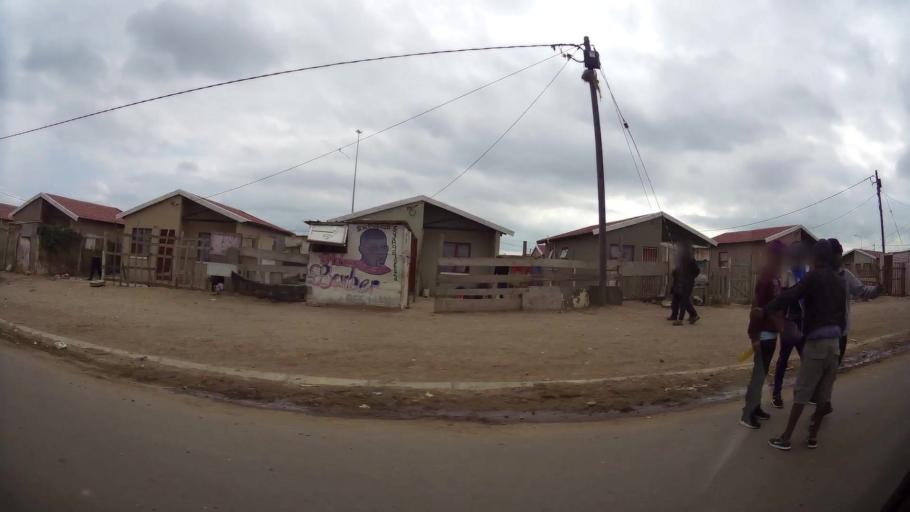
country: ZA
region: Eastern Cape
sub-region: Nelson Mandela Bay Metropolitan Municipality
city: Port Elizabeth
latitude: -33.8817
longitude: 25.5520
